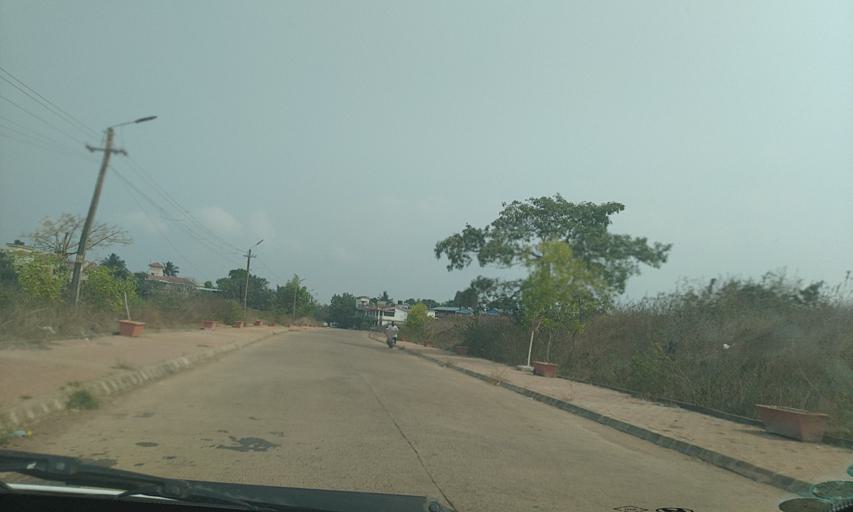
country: IN
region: Goa
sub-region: North Goa
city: Taleigao
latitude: 15.4605
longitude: 73.8175
